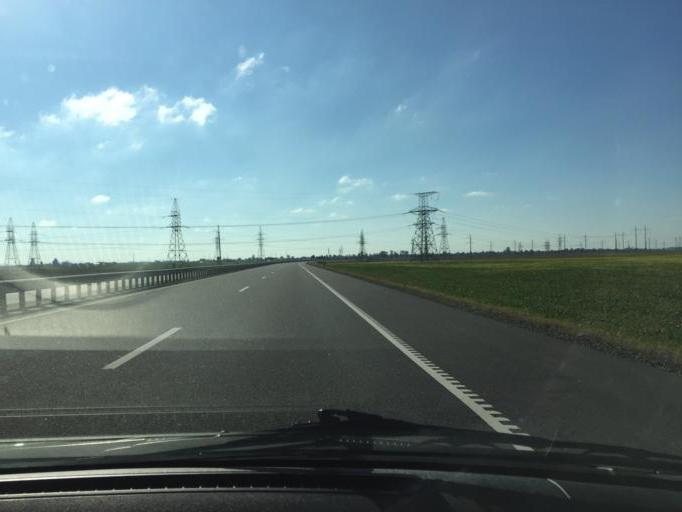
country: BY
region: Minsk
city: Slutsk
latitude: 53.0592
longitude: 27.5441
